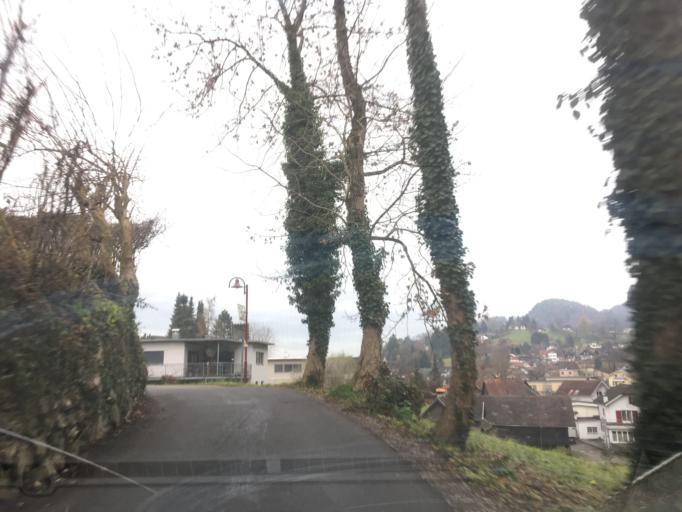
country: AT
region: Vorarlberg
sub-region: Politischer Bezirk Feldkirch
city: Gotzis
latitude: 47.3301
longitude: 9.6464
